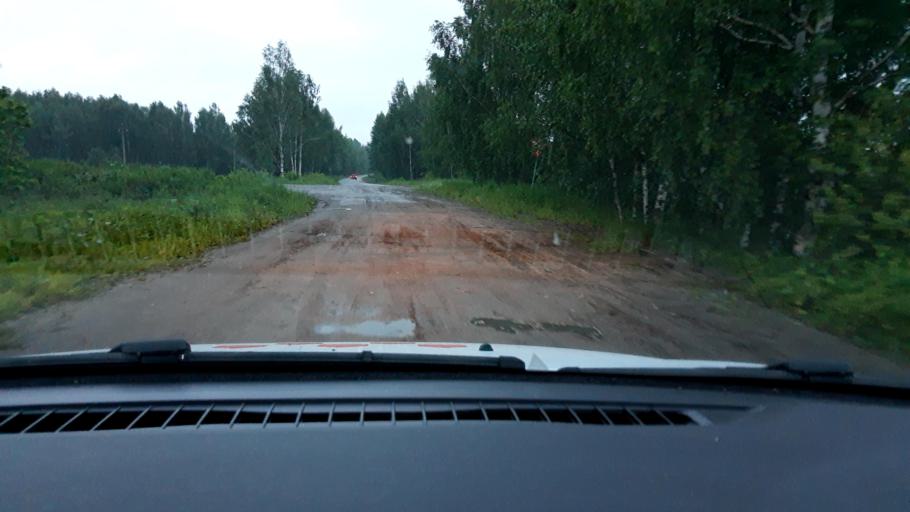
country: RU
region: Nizjnij Novgorod
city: Novaya Balakhna
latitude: 56.6342
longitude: 43.6270
